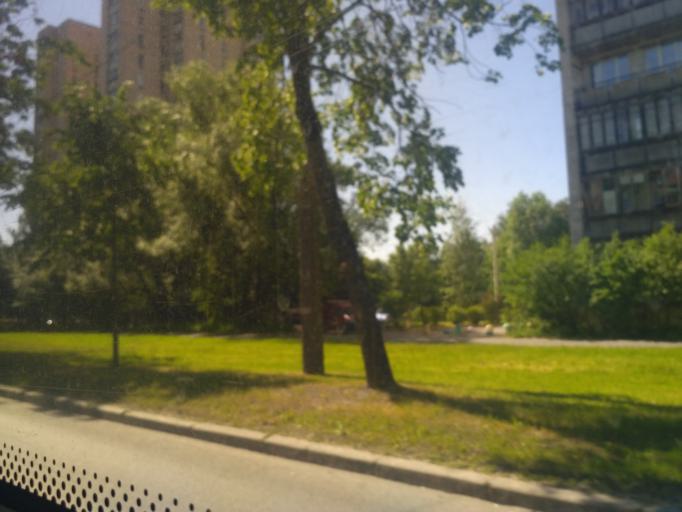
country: RU
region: Leningrad
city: Kalininskiy
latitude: 59.9677
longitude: 30.4125
